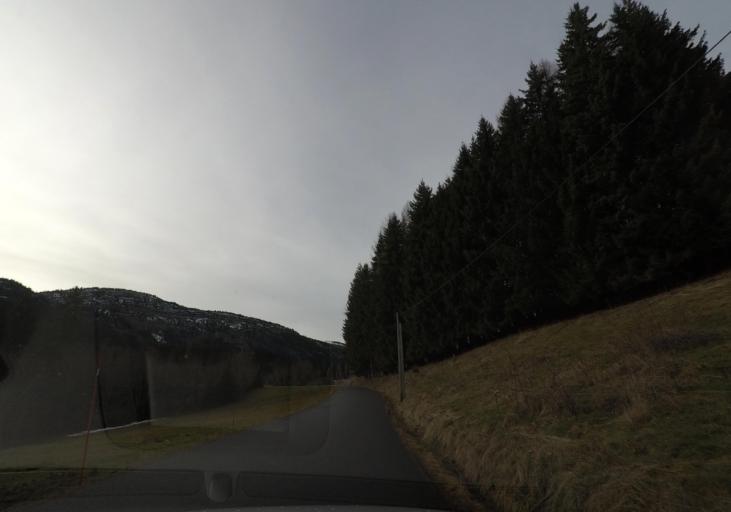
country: FR
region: Rhone-Alpes
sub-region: Departement de la Haute-Savoie
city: Ayse
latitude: 46.0377
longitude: 6.4416
